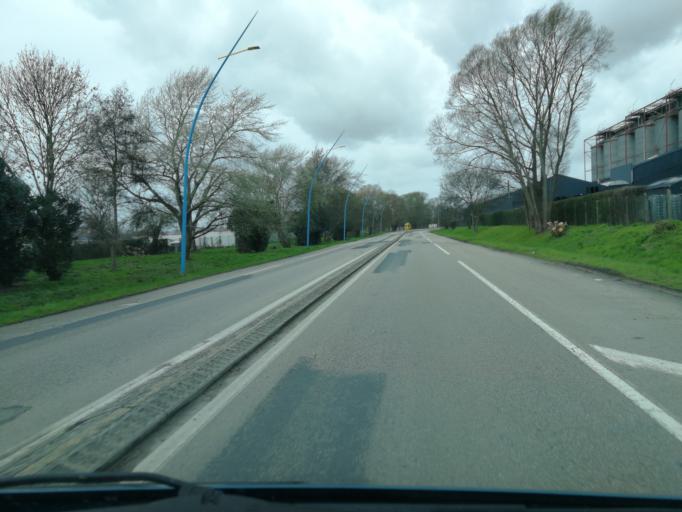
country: FR
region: Haute-Normandie
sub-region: Departement de l'Eure
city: Quillebeuf-sur-Seine
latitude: 49.4750
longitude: 0.5346
